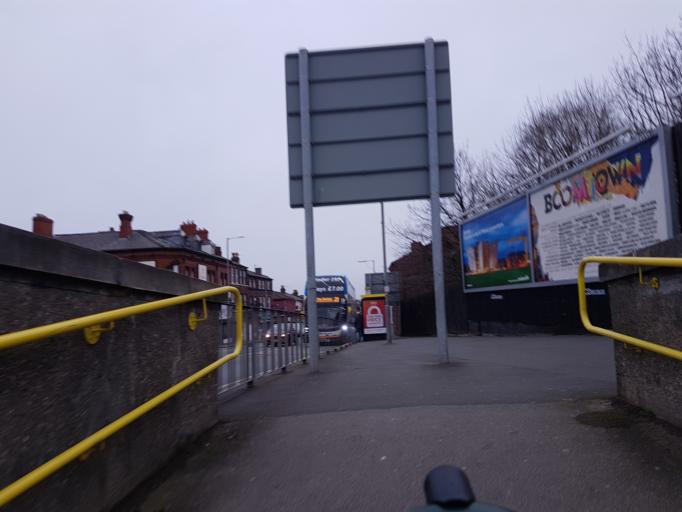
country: GB
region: England
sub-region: Sefton
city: Litherland
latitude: 53.4481
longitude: -2.9667
